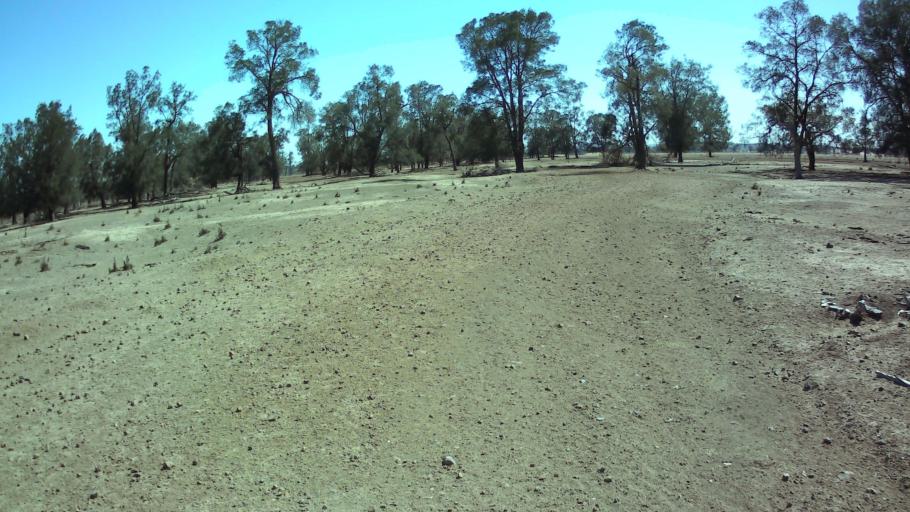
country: AU
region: New South Wales
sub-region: Bland
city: West Wyalong
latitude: -33.7622
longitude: 147.6585
